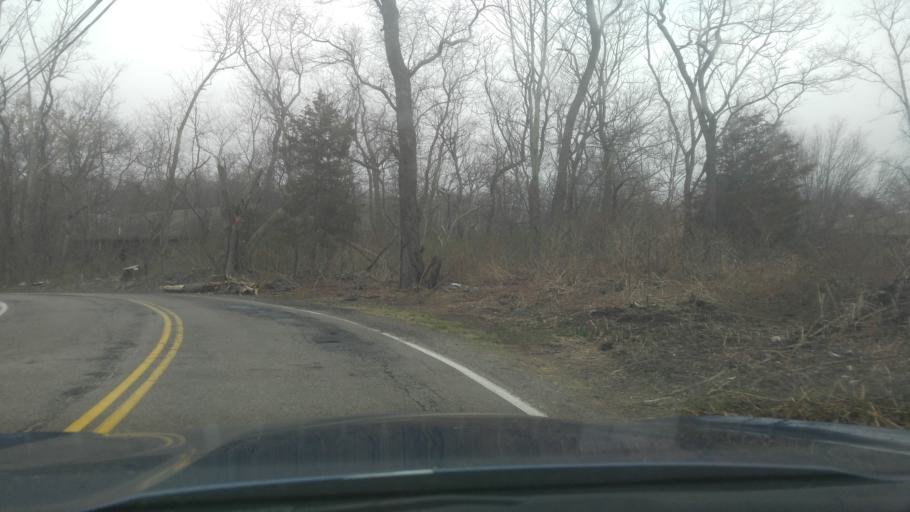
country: US
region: Rhode Island
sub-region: Kent County
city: East Greenwich
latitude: 41.6901
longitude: -71.4793
